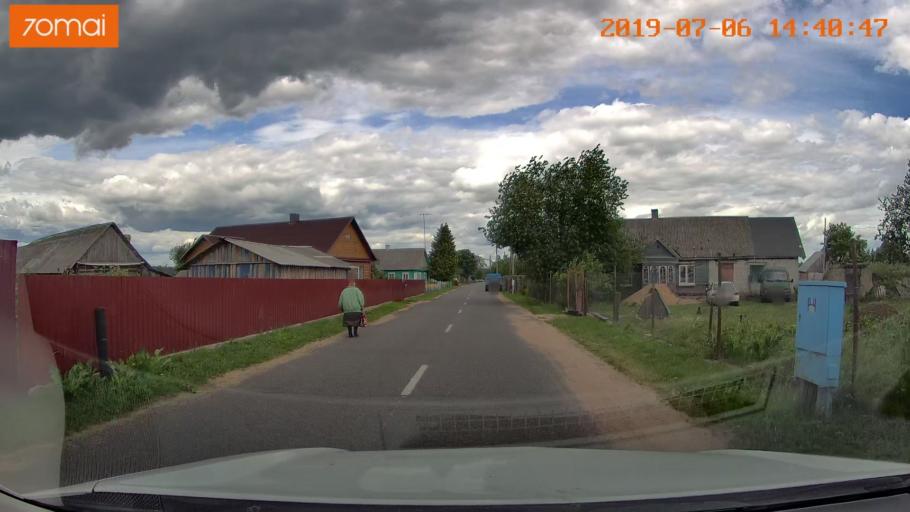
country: BY
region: Minsk
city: Ivyanyets
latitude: 53.9265
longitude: 26.6737
